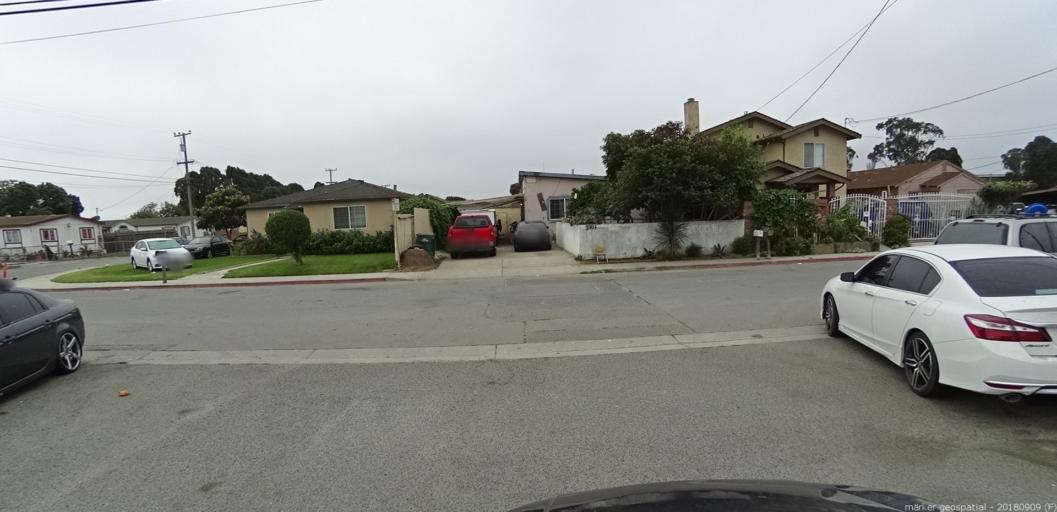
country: US
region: California
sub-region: Monterey County
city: Boronda
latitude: 36.6960
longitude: -121.6726
